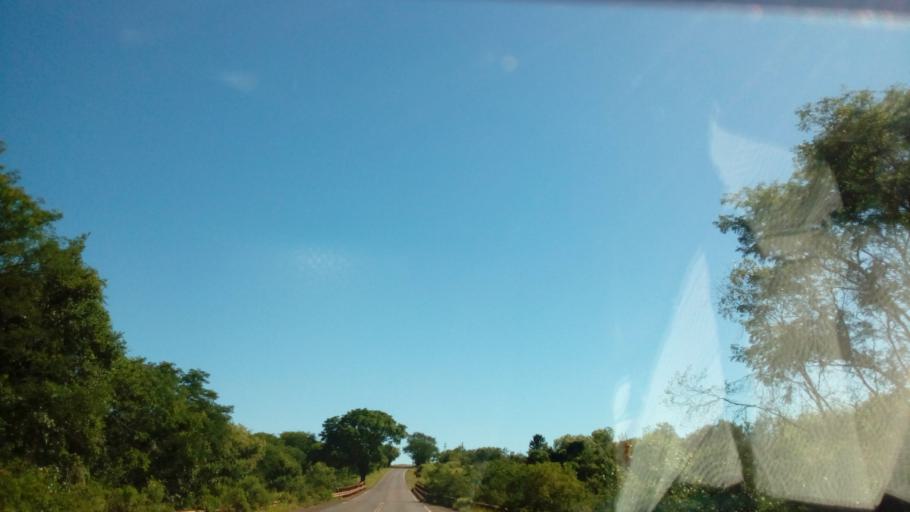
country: AR
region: Misiones
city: Cerro Cora
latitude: -27.4429
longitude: -55.6476
